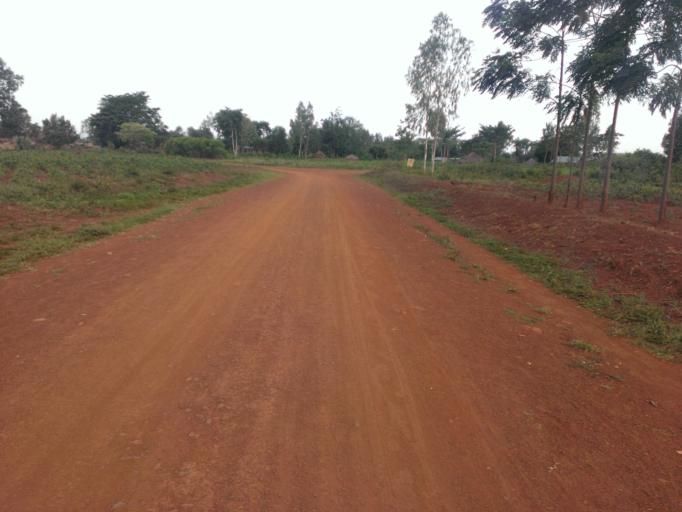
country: UG
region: Eastern Region
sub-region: Busia District
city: Busia
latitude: 0.5292
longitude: 34.0405
